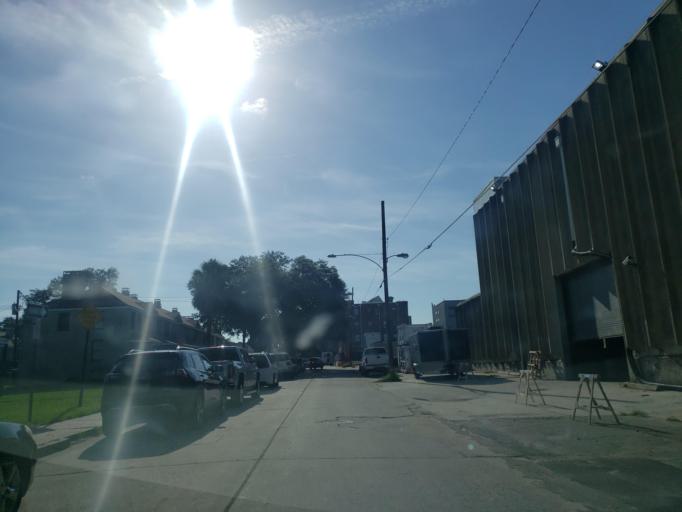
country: US
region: Georgia
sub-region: Chatham County
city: Savannah
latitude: 32.0807
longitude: -81.0995
